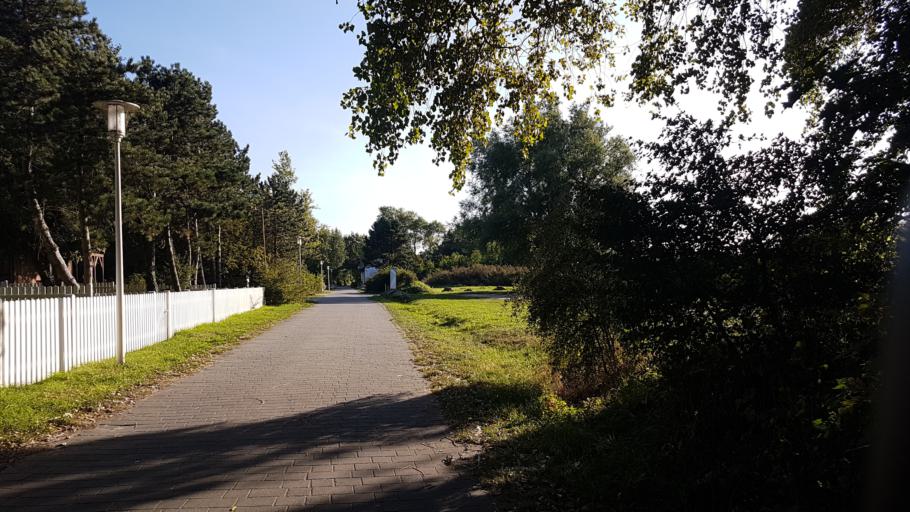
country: DE
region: Mecklenburg-Vorpommern
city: Wiek
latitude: 54.6321
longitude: 13.2896
